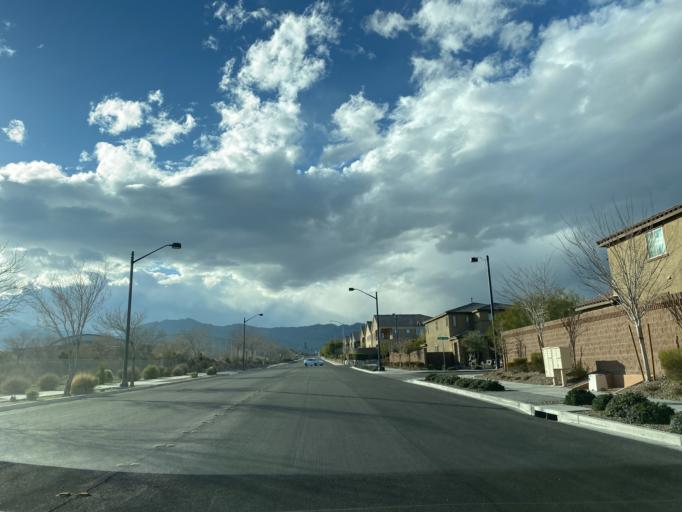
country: US
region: Nevada
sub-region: Clark County
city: Summerlin South
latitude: 36.2828
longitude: -115.3002
